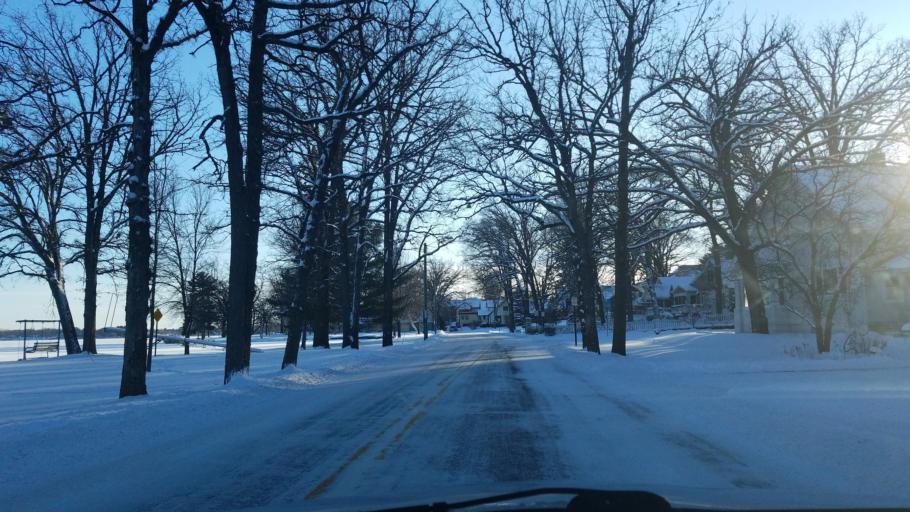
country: US
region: Wisconsin
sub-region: Barron County
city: Rice Lake
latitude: 45.5068
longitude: -91.7314
